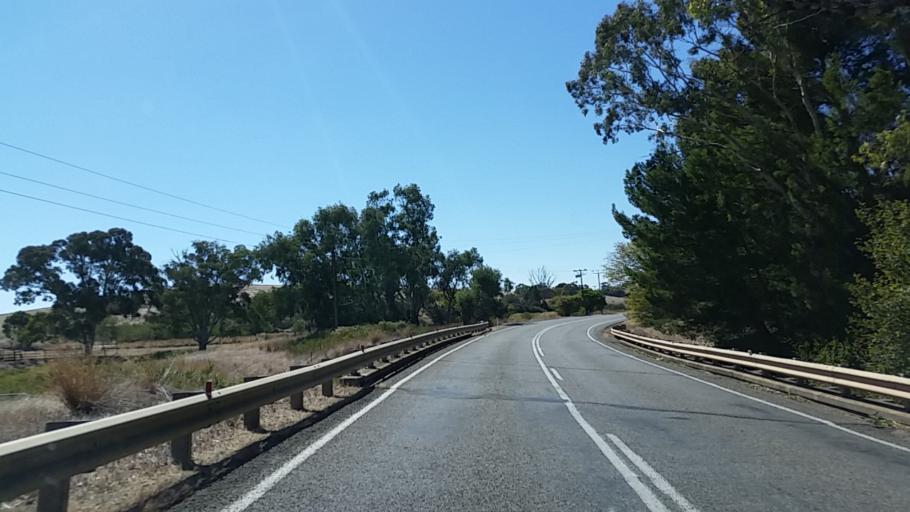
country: AU
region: South Australia
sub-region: Light
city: Kapunda
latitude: -34.0891
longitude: 138.7756
